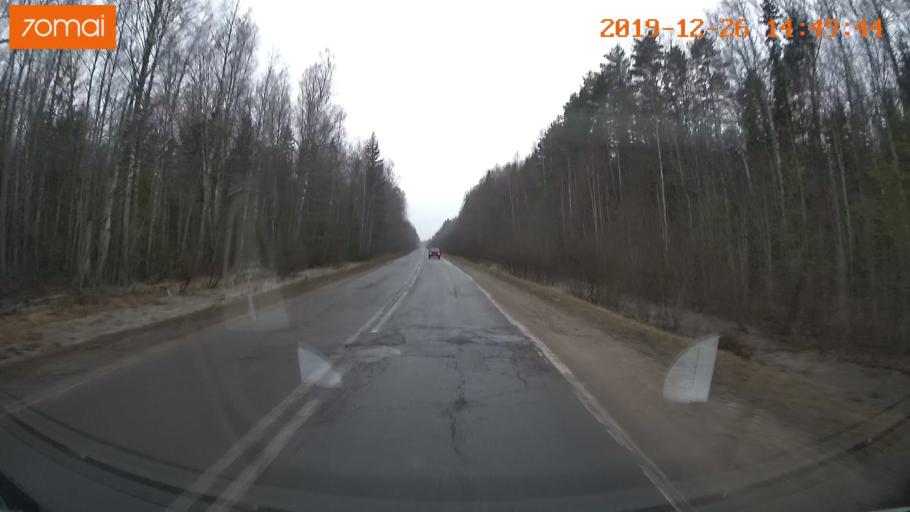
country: RU
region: Jaroslavl
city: Poshekhon'ye
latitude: 58.3375
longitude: 38.9381
